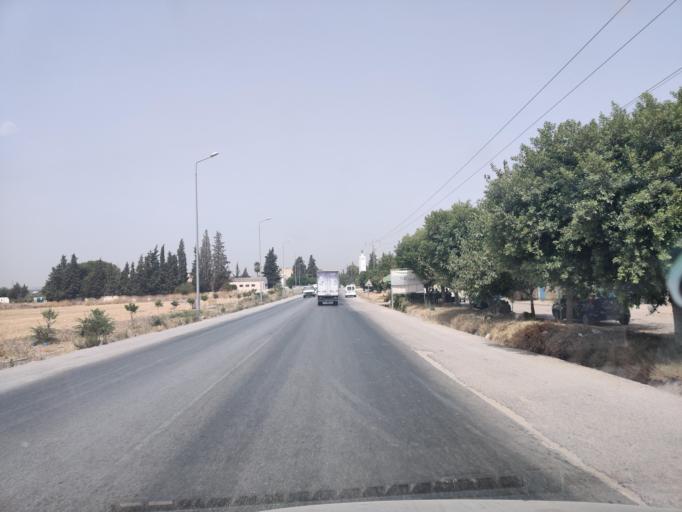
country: TN
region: Tunis
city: La Sebala du Mornag
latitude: 36.6605
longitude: 10.3270
